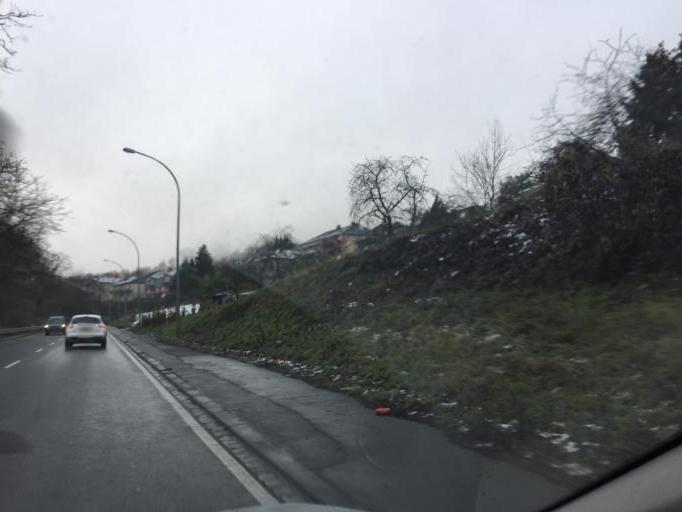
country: LU
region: Diekirch
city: Warken
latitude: 49.8500
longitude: 6.0779
